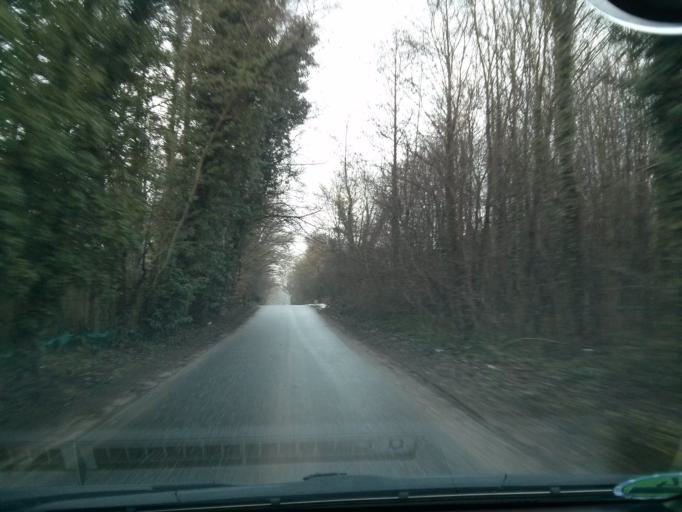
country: DE
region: North Rhine-Westphalia
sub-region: Regierungsbezirk Koln
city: Alfter
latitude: 50.6827
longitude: 7.0000
